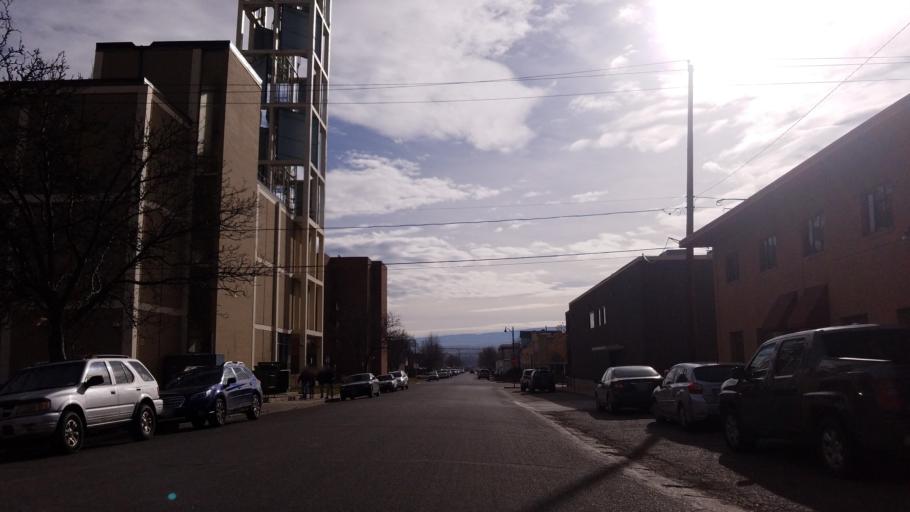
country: US
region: Colorado
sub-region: Mesa County
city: Grand Junction
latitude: 39.0681
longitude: -108.5594
